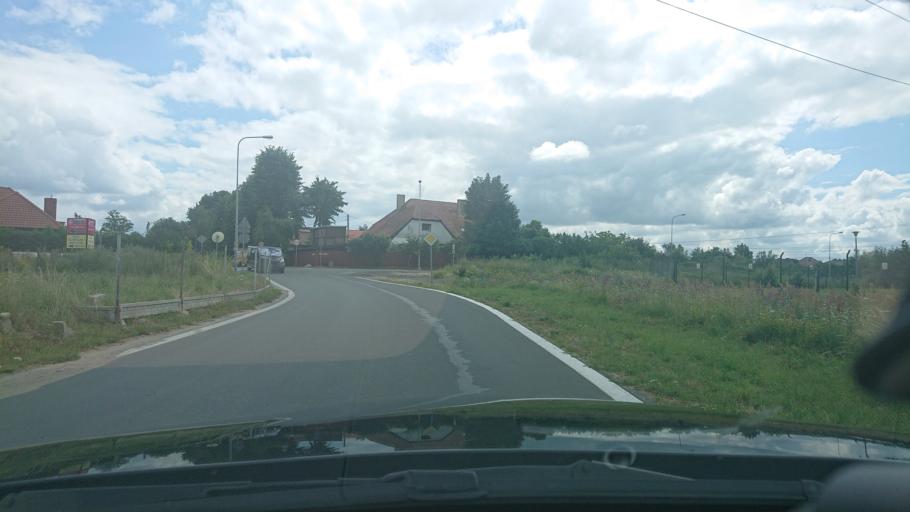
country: PL
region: Greater Poland Voivodeship
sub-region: Powiat gnieznienski
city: Gniezno
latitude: 52.5168
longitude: 17.6225
